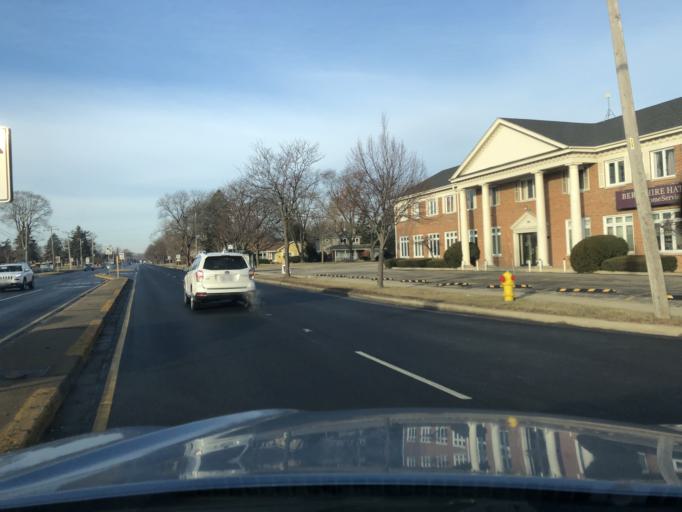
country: US
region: Illinois
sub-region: Cook County
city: Mount Prospect
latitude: 42.0476
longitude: -87.9407
